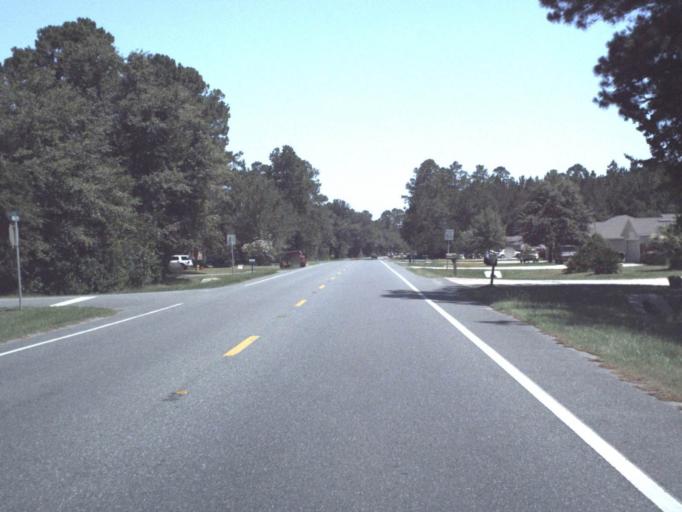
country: US
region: Florida
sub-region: Baker County
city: Macclenny
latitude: 30.2913
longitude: -82.1257
